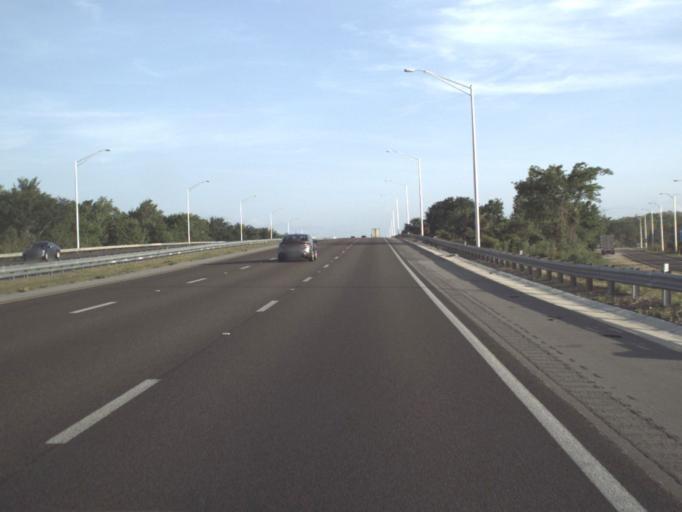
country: US
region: Florida
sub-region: Volusia County
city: Oak Hill
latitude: 28.7741
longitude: -80.8949
